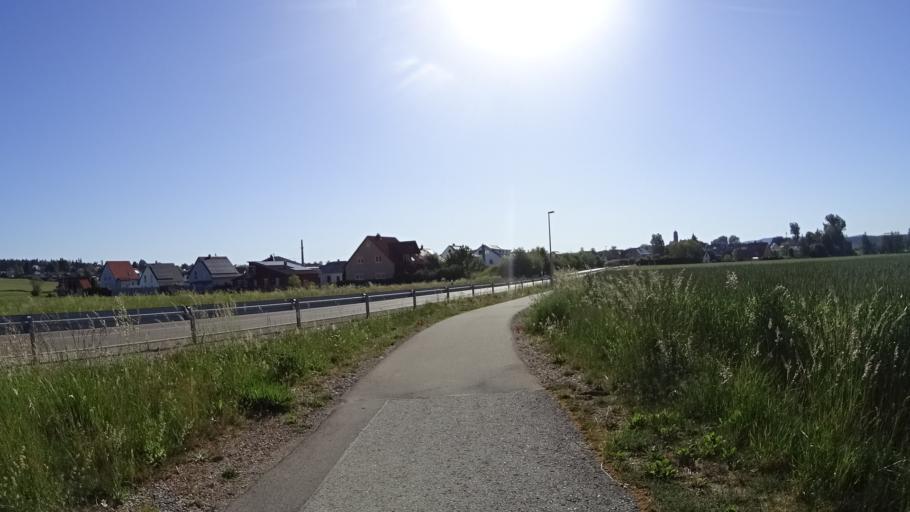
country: DE
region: Bavaria
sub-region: Regierungsbezirk Mittelfranken
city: Wieseth
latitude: 49.1592
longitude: 10.5416
